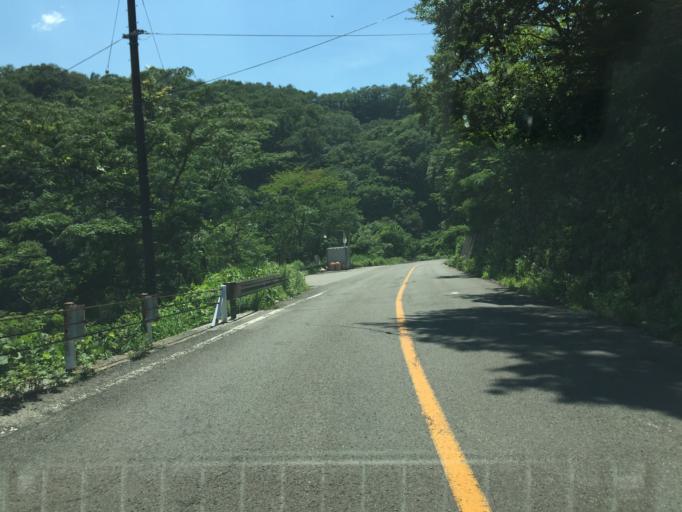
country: JP
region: Fukushima
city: Fukushima-shi
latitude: 37.7496
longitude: 140.3240
